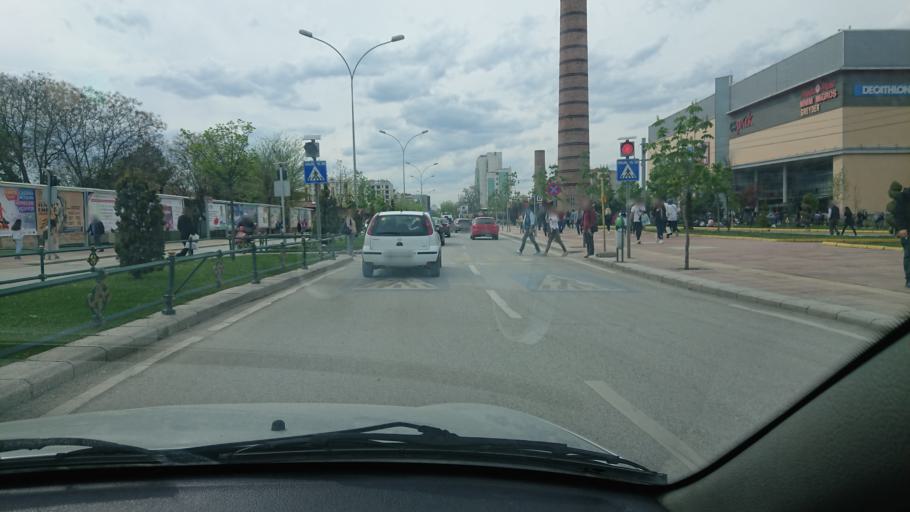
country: TR
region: Eskisehir
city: Eskisehir
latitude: 39.7809
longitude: 30.5108
